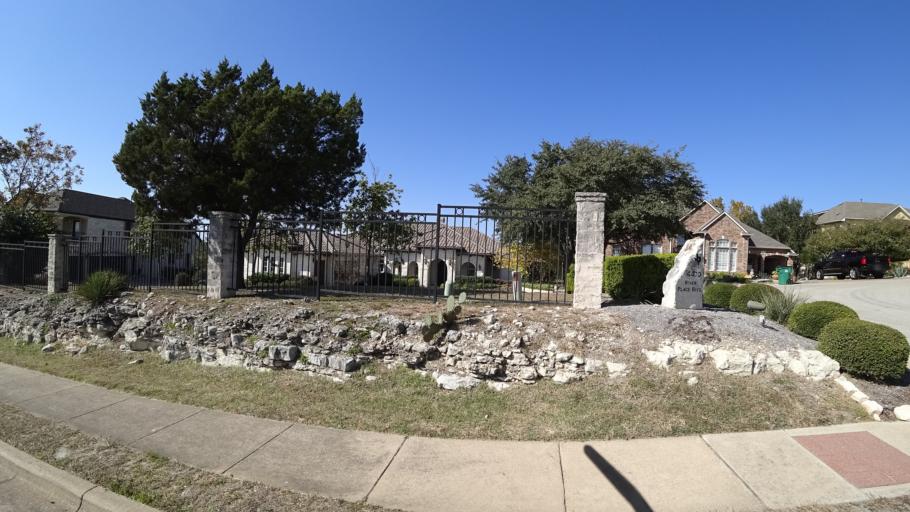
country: US
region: Texas
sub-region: Travis County
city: Lost Creek
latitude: 30.3711
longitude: -97.8603
